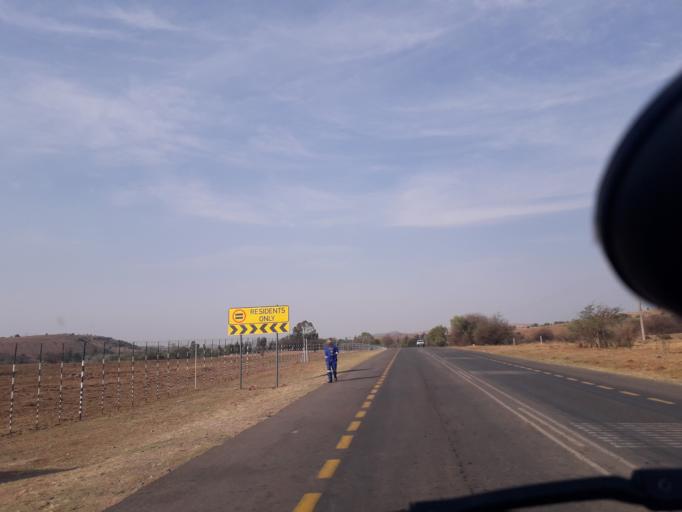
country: ZA
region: Gauteng
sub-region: West Rand District Municipality
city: Krugersdorp
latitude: -26.0124
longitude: 27.7383
